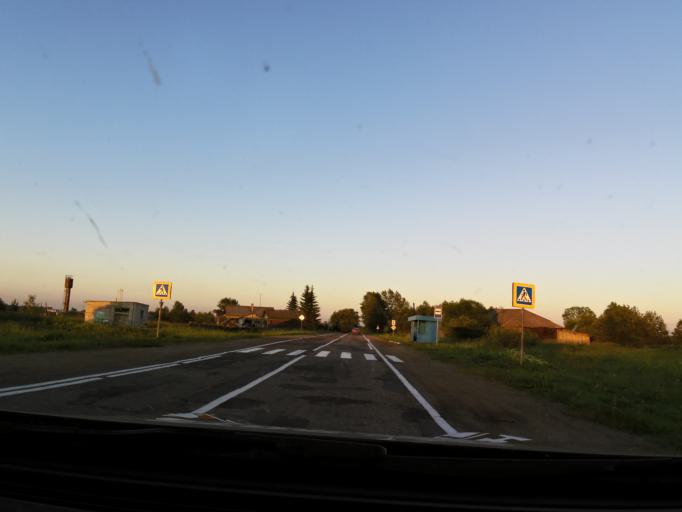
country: RU
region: Jaroslavl
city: Lyubim
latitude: 58.3567
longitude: 40.6521
